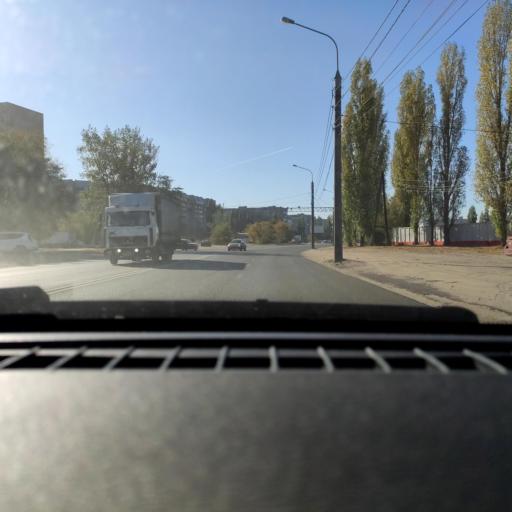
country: RU
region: Voronezj
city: Voronezh
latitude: 51.6449
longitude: 39.2672
